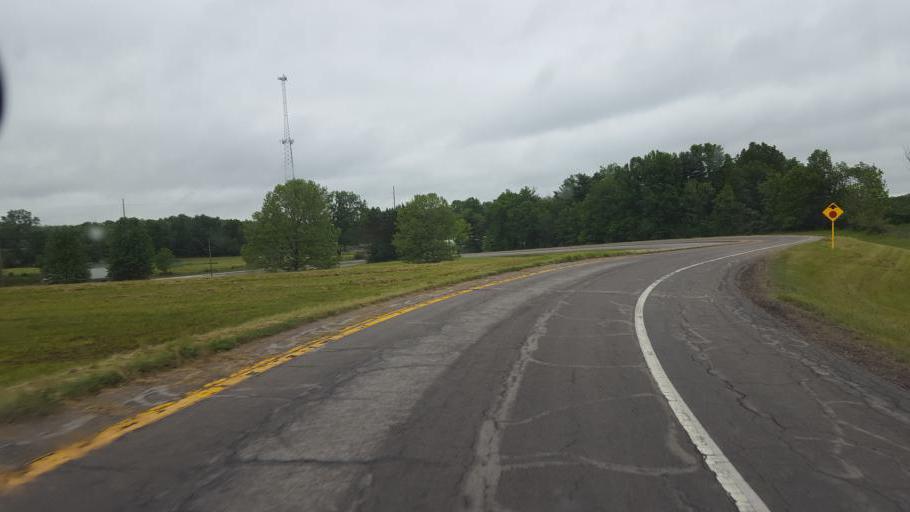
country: US
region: Ohio
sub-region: Medina County
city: Lodi
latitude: 41.0250
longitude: -82.0515
